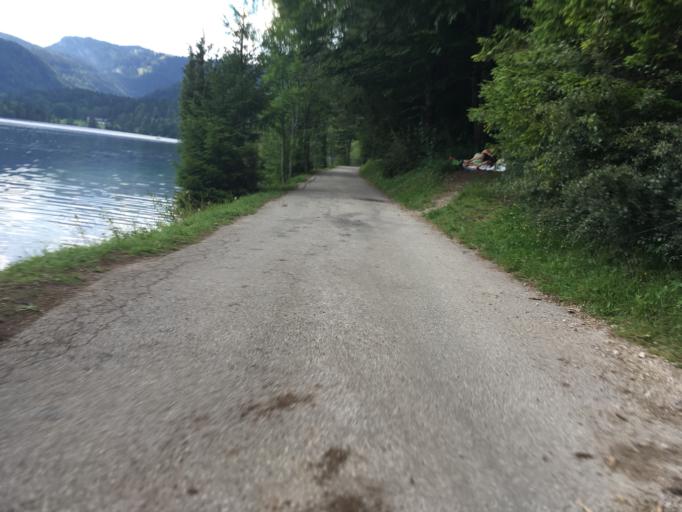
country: AT
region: Lower Austria
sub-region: Politischer Bezirk Lilienfeld
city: Mitterbach am Erlaufsee
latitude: 47.7936
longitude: 15.2753
